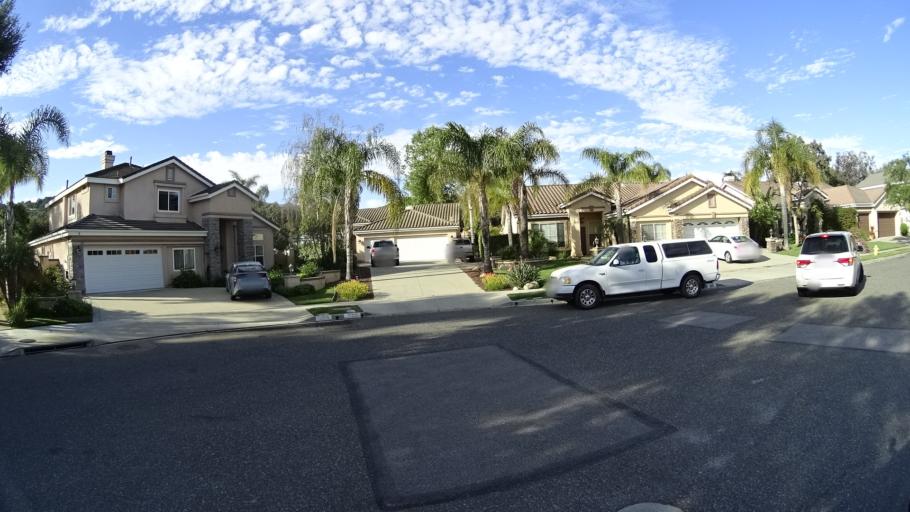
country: US
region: California
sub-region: Ventura County
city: Casa Conejo
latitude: 34.1745
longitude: -118.9473
